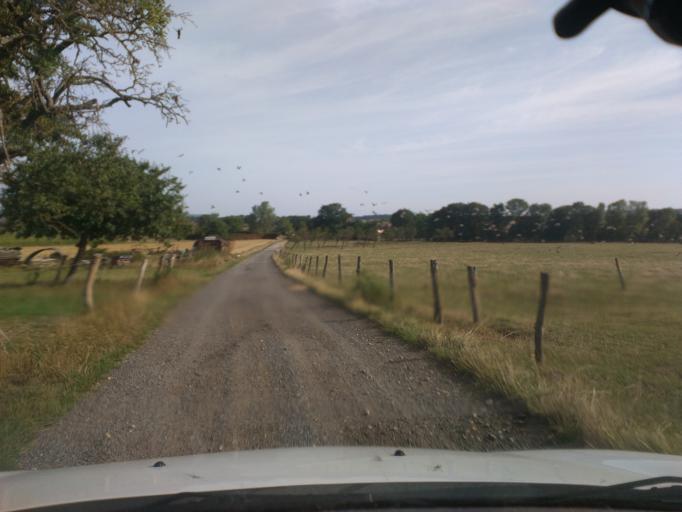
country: FR
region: Lorraine
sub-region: Departement des Vosges
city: Mirecourt
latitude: 48.3289
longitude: 6.0951
